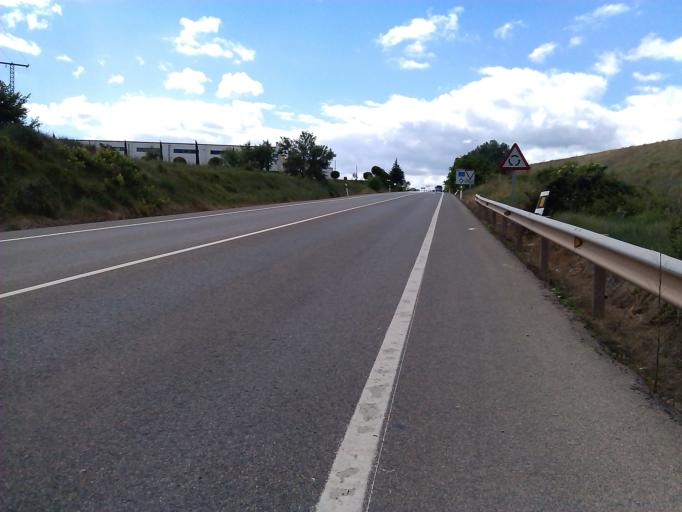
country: ES
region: La Rioja
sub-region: Provincia de La Rioja
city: Najera
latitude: 42.4257
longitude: -2.7409
